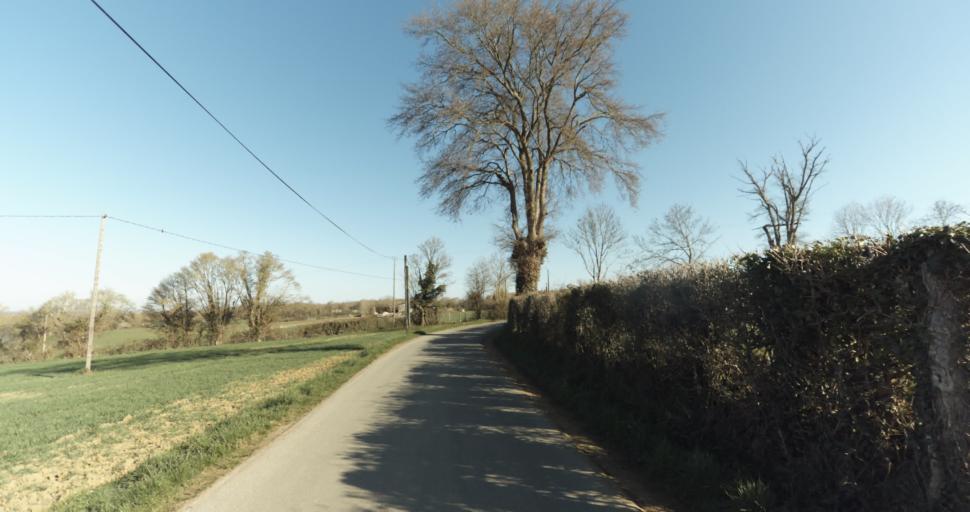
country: FR
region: Lower Normandy
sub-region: Departement du Calvados
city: Saint-Pierre-sur-Dives
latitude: 48.9902
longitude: -0.0012
